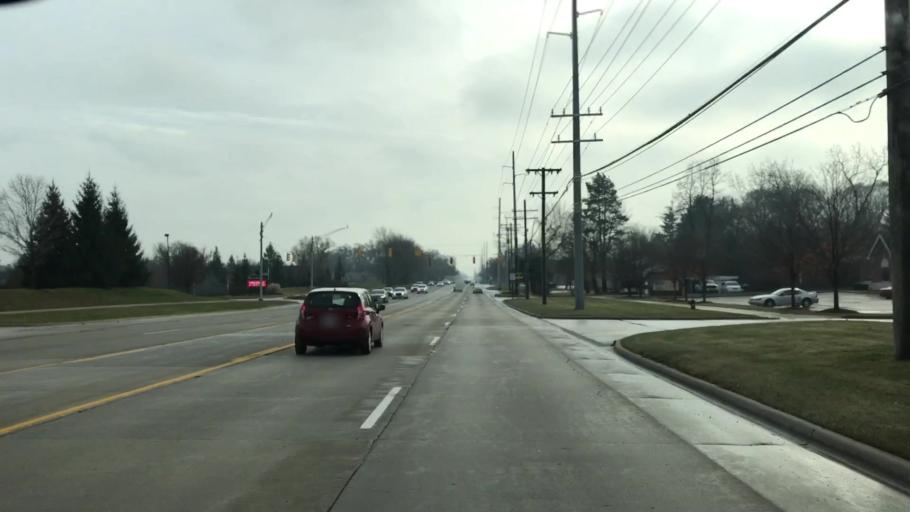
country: US
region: Michigan
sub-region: Oakland County
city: Troy
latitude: 42.6168
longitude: -83.1304
